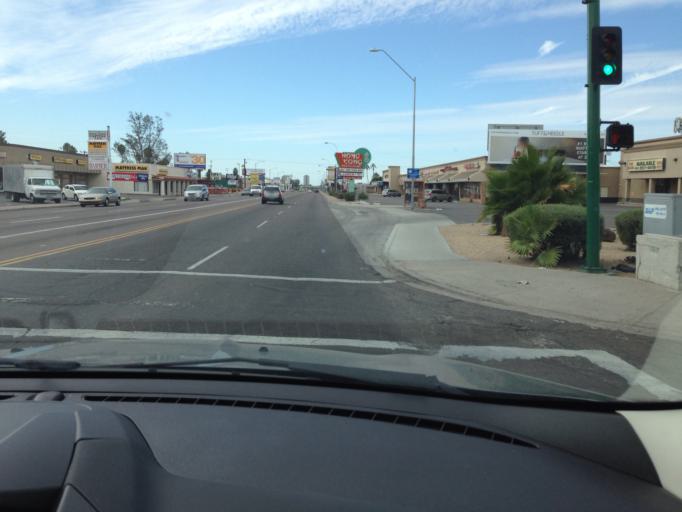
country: US
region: Arizona
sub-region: Maricopa County
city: Phoenix
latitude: 33.4949
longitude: -112.0301
